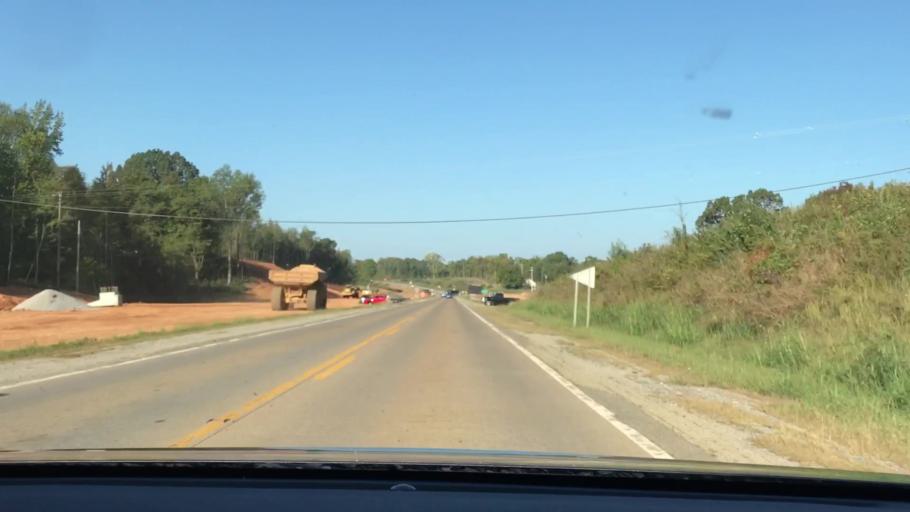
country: US
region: Kentucky
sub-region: Trigg County
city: Cadiz
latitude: 36.7987
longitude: -87.9531
